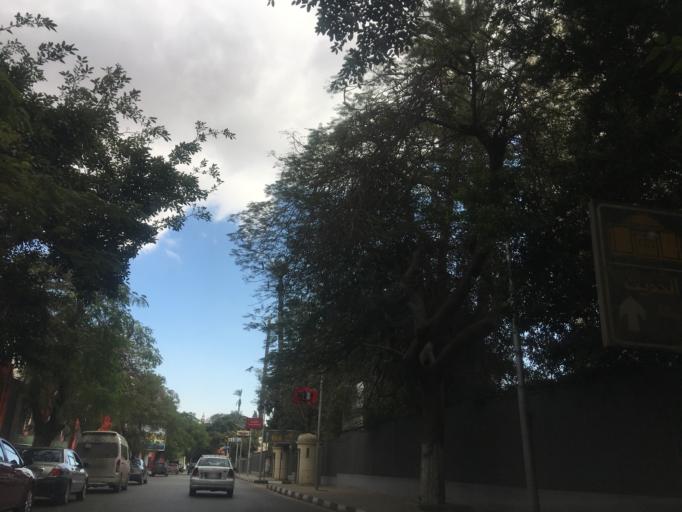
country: EG
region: Muhafazat al Qahirah
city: Cairo
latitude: 30.0441
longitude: 31.2213
